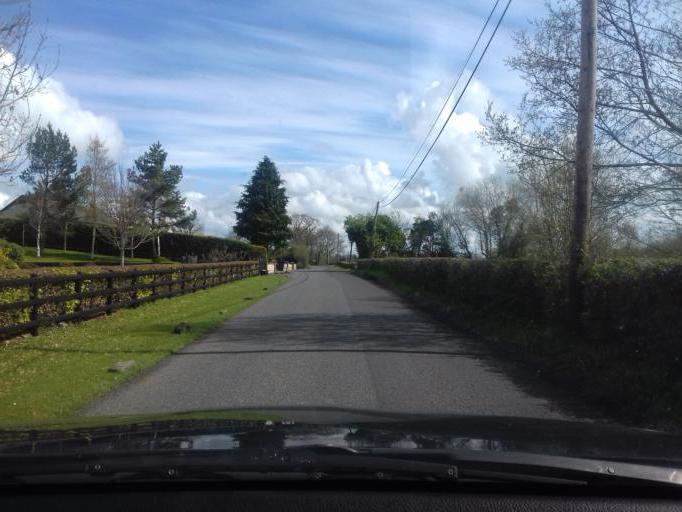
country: IE
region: Ulster
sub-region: An Cabhan
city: Ballyconnell
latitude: 54.1620
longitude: -7.5146
